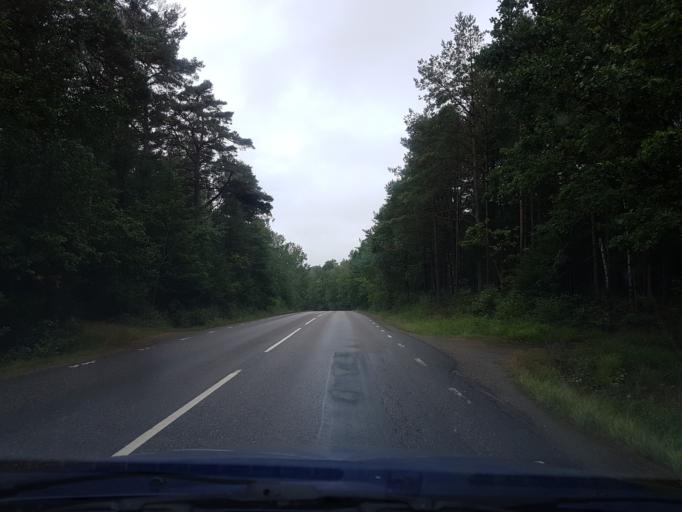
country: SE
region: Vaestra Goetaland
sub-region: Ale Kommun
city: Skepplanda
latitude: 57.9472
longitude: 12.1936
